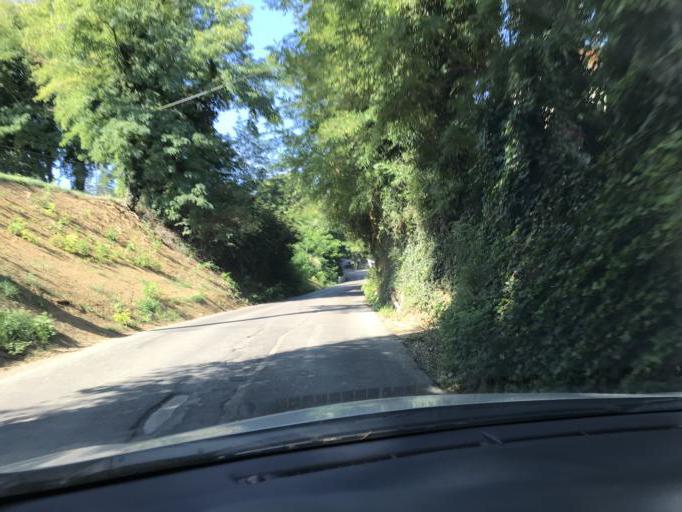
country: IT
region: Umbria
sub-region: Provincia di Perugia
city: Ponte Felcino
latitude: 43.1062
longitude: 12.4392
